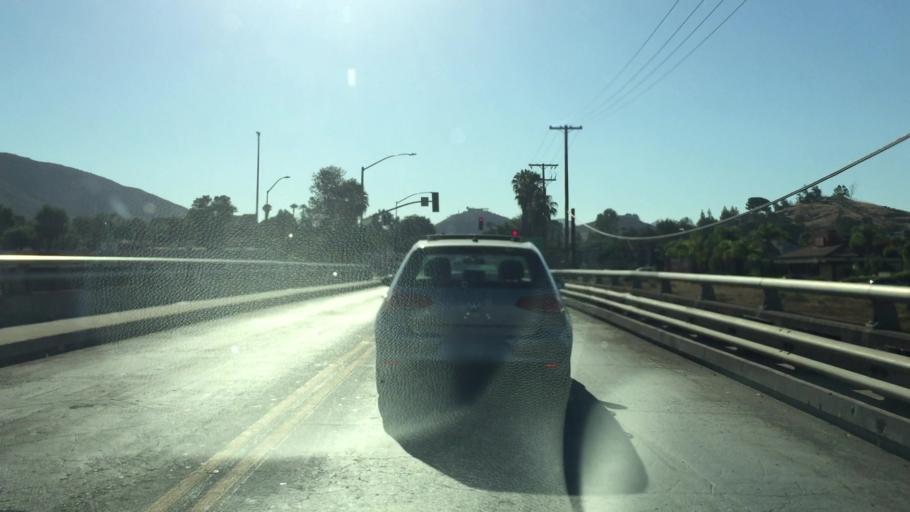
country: US
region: California
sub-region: San Diego County
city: El Cajon
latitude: 32.8177
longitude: -116.9595
